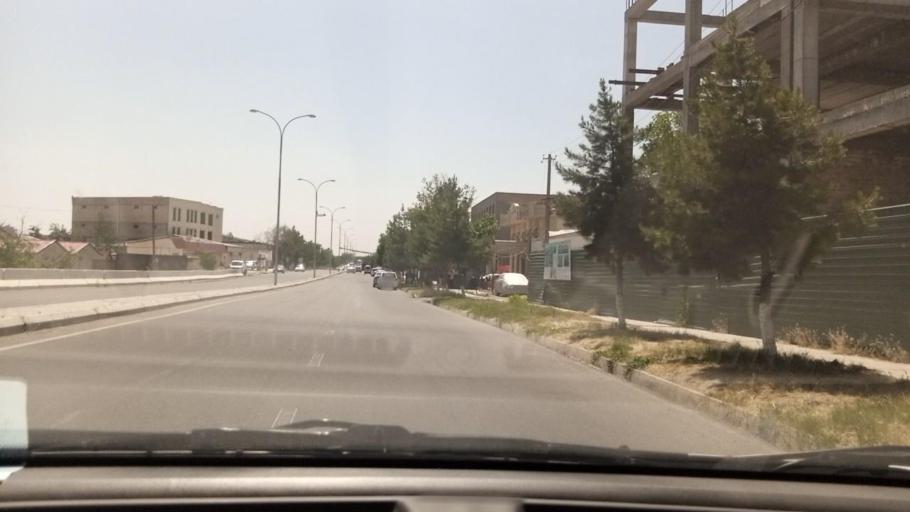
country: UZ
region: Toshkent Shahri
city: Tashkent
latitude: 41.2453
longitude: 69.2031
